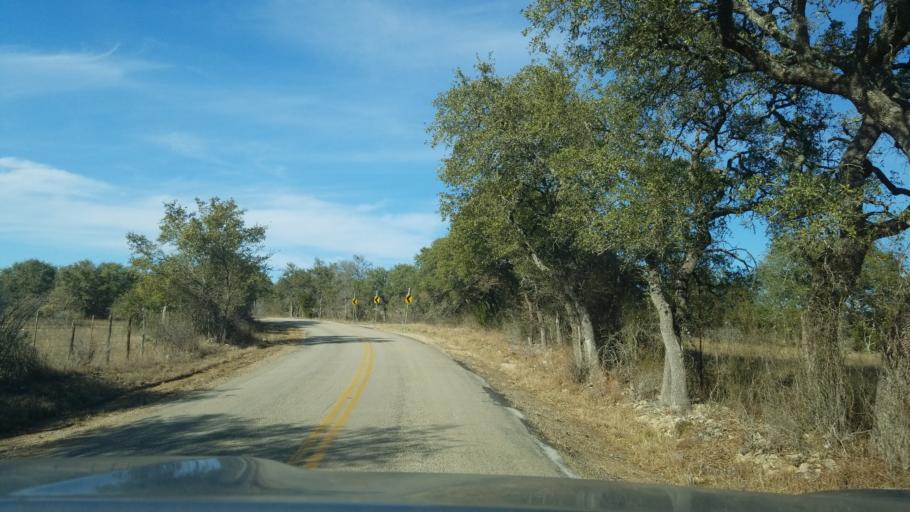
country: US
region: Texas
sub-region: Comal County
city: Canyon Lake
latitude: 29.7901
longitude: -98.2879
